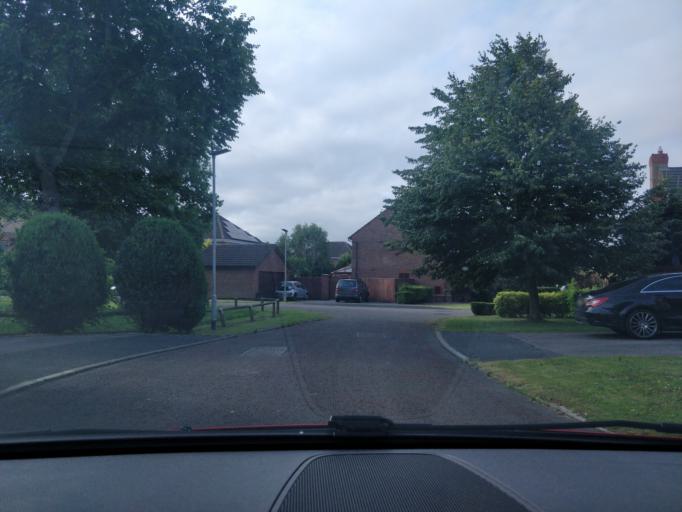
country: GB
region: England
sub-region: Lancashire
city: Banks
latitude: 53.6754
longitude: -2.9130
